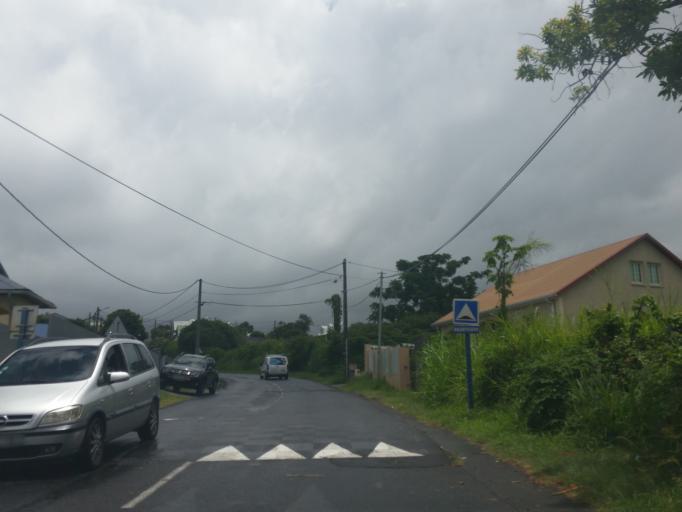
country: RE
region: Reunion
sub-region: Reunion
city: Le Tampon
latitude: -21.2505
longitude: 55.5049
